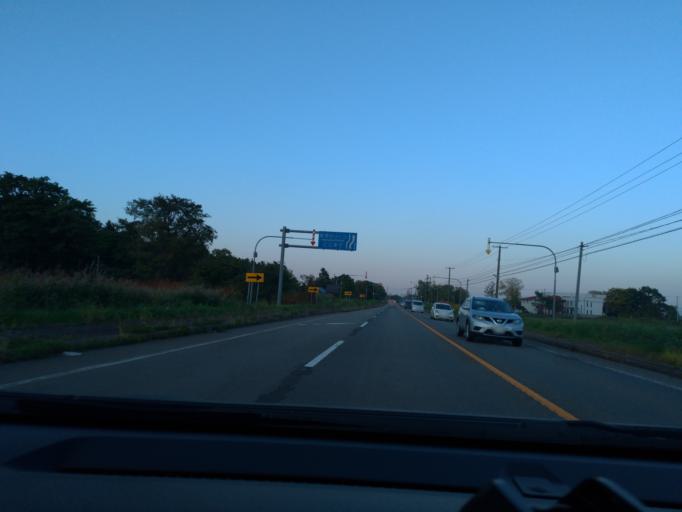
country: JP
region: Hokkaido
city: Tobetsu
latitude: 43.3204
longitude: 141.6103
